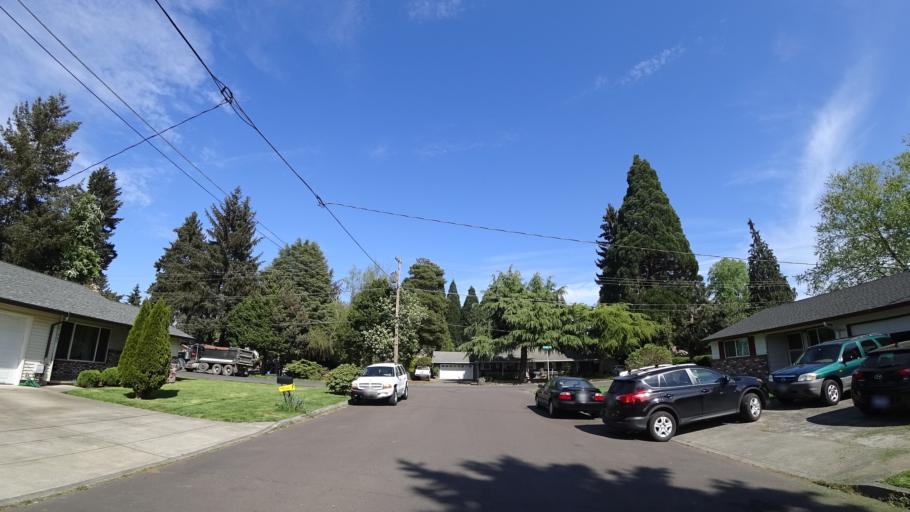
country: US
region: Oregon
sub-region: Washington County
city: Aloha
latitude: 45.4997
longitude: -122.8971
